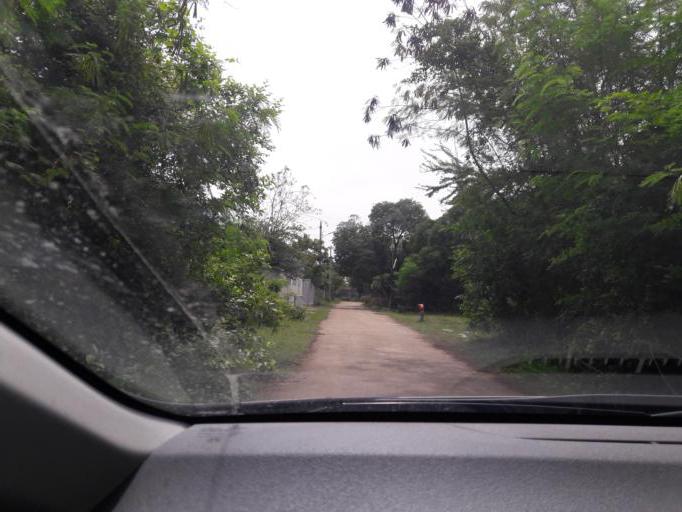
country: TH
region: Ratchaburi
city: Ratchaburi
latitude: 13.5186
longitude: 99.7942
